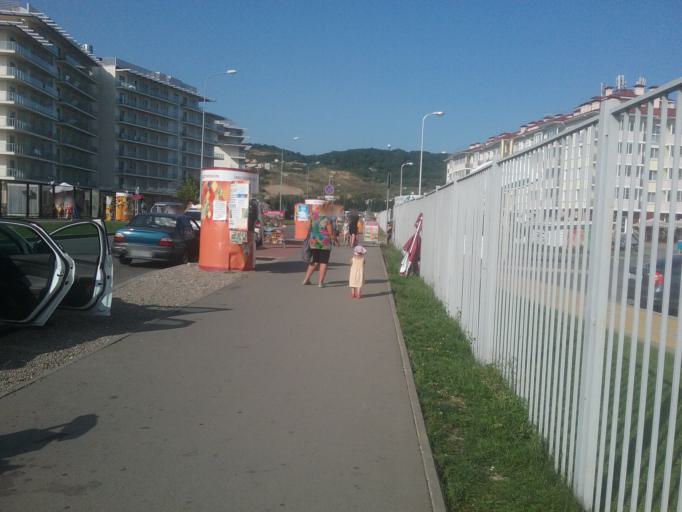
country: RU
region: Krasnodarskiy
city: Adler
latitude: 43.4012
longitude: 39.9778
